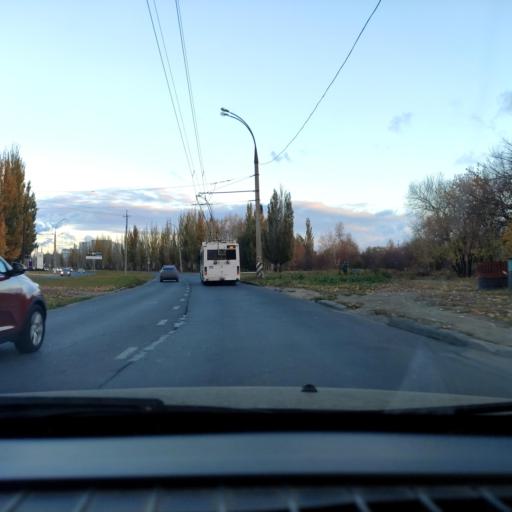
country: RU
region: Samara
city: Tol'yatti
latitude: 53.5426
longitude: 49.2793
